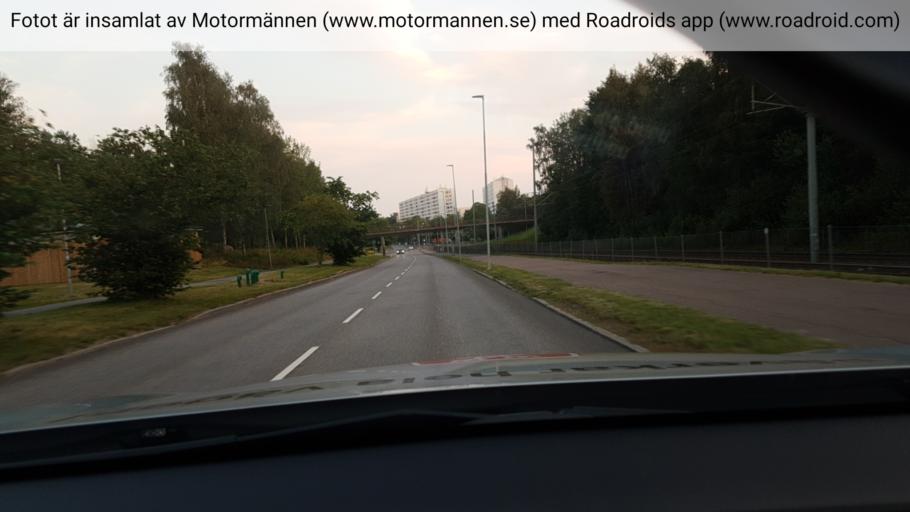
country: SE
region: Vaestra Goetaland
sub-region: Goteborg
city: Majorna
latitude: 57.7295
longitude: 11.8945
